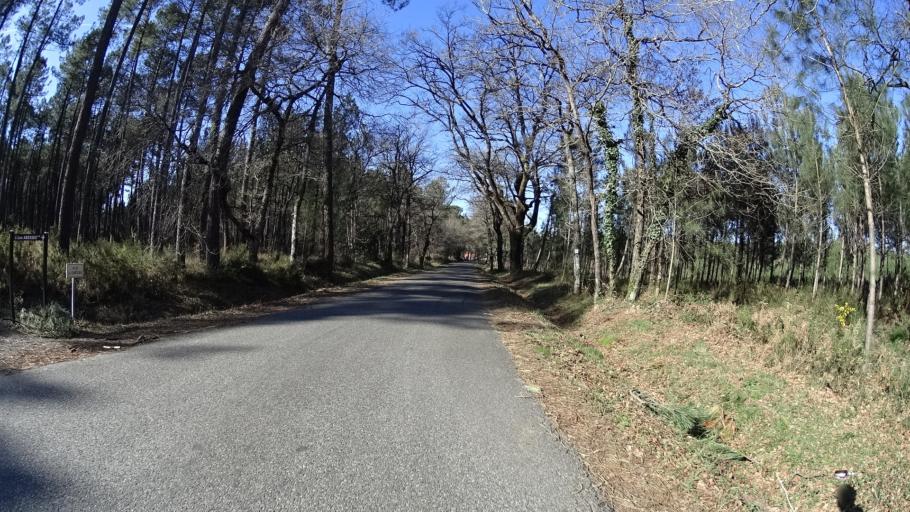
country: FR
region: Aquitaine
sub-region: Departement des Landes
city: Mees
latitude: 43.7397
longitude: -1.0966
